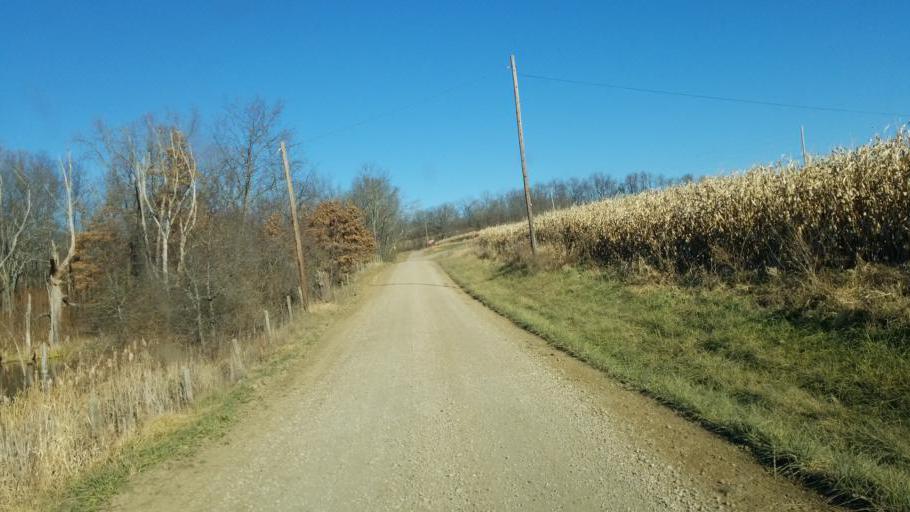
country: US
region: Ohio
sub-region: Muskingum County
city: Dresden
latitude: 40.1057
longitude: -81.9513
